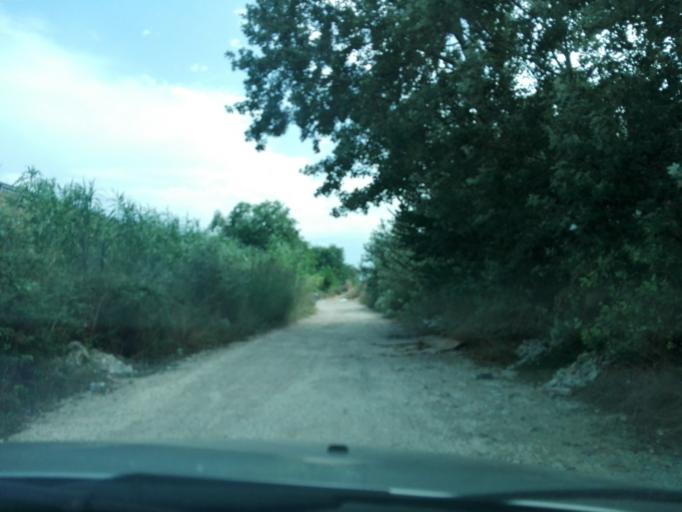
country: IT
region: Abruzzo
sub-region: Provincia di Pescara
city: Cappelle sul Tavo
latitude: 42.4890
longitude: 14.1115
